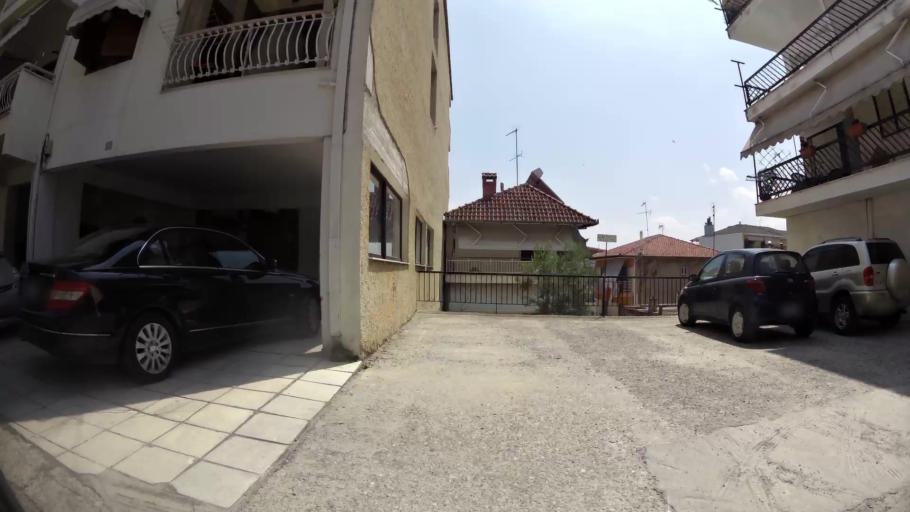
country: GR
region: Central Macedonia
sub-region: Nomos Imathias
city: Veroia
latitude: 40.5160
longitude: 22.2053
